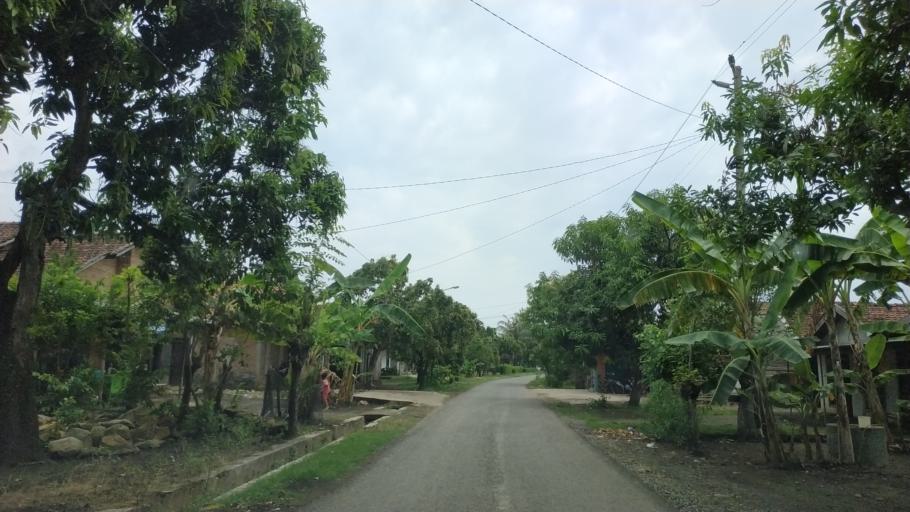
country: ID
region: Central Java
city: Krajan Tegalombo
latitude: -6.4230
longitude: 110.9834
